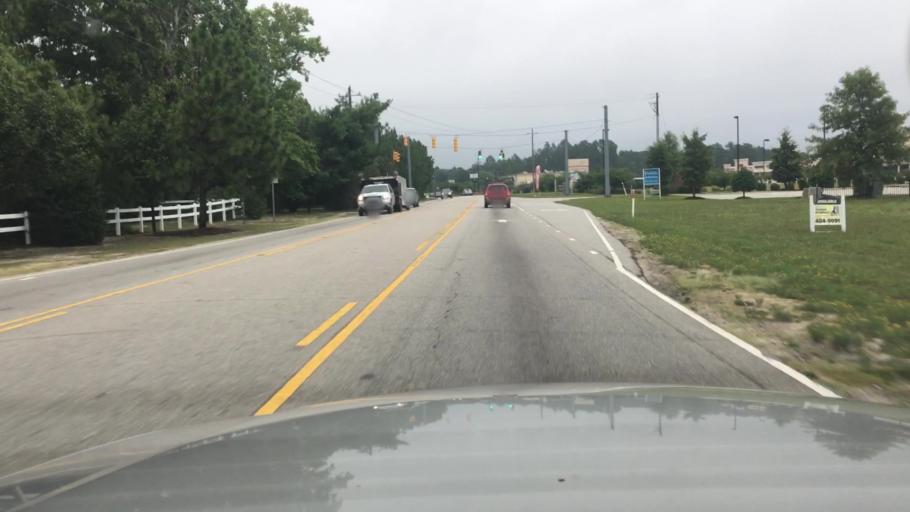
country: US
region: North Carolina
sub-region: Cumberland County
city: Hope Mills
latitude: 34.9803
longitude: -78.9772
